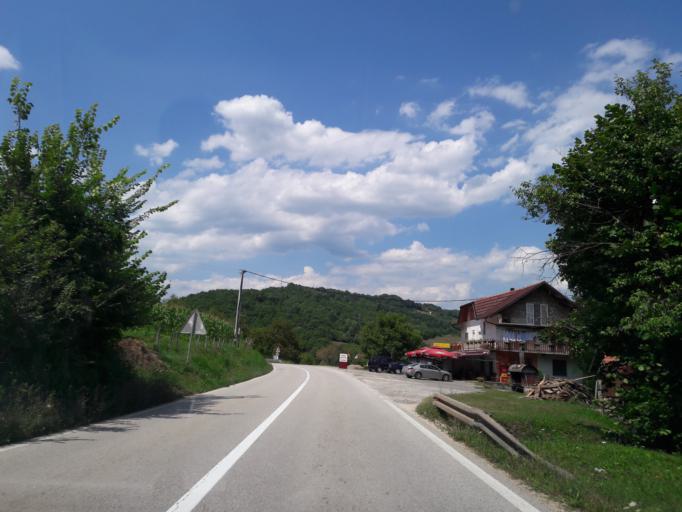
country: BA
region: Republika Srpska
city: Mrkonjic Grad
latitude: 44.5375
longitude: 17.1492
